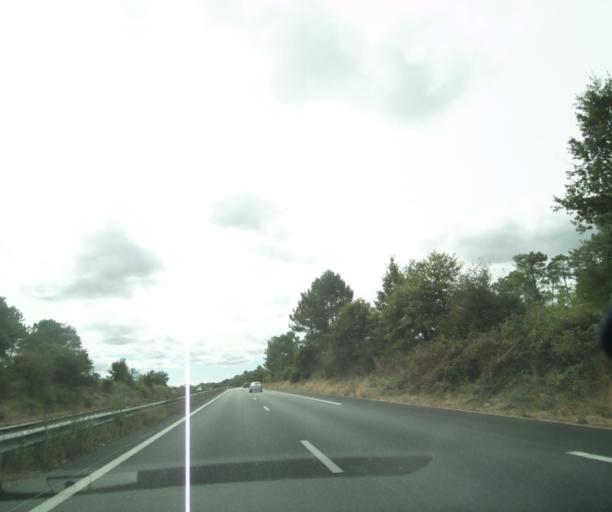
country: FR
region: Aquitaine
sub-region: Departement de la Gironde
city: Reignac
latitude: 45.2144
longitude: -0.5063
